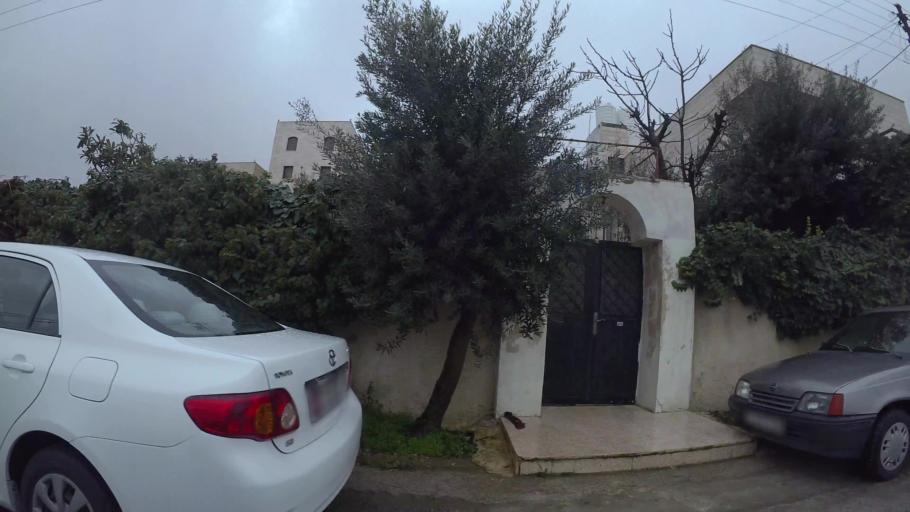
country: JO
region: Amman
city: Al Jubayhah
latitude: 32.0193
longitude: 35.8328
